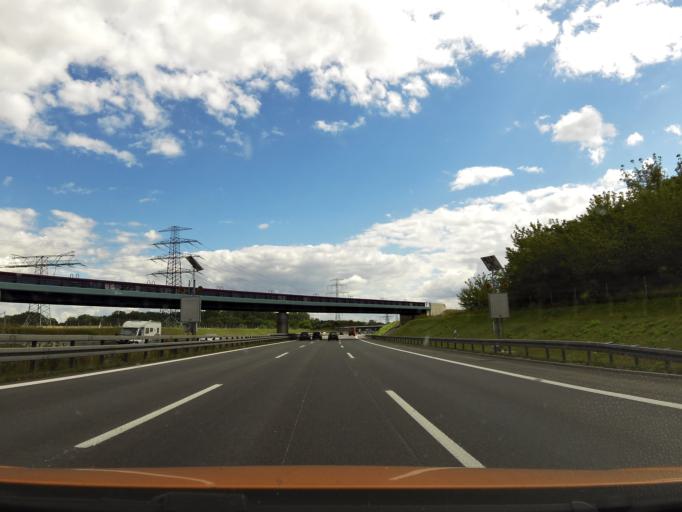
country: DE
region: Berlin
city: Karow
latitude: 52.6283
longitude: 13.4746
